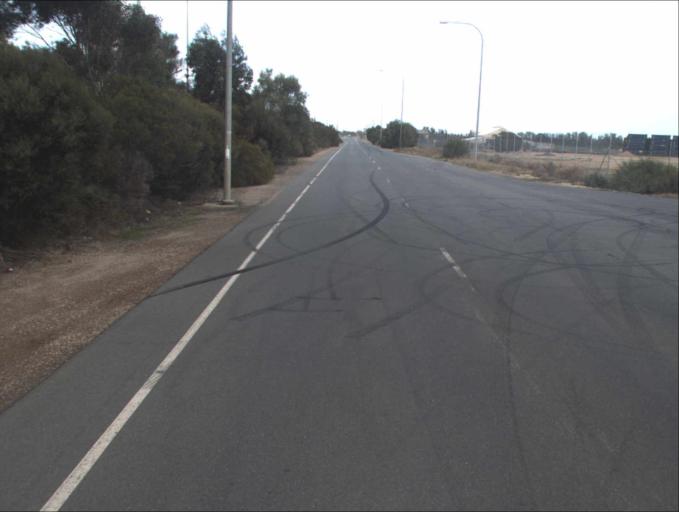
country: AU
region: South Australia
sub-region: Port Adelaide Enfield
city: Birkenhead
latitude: -34.7695
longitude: 138.5016
